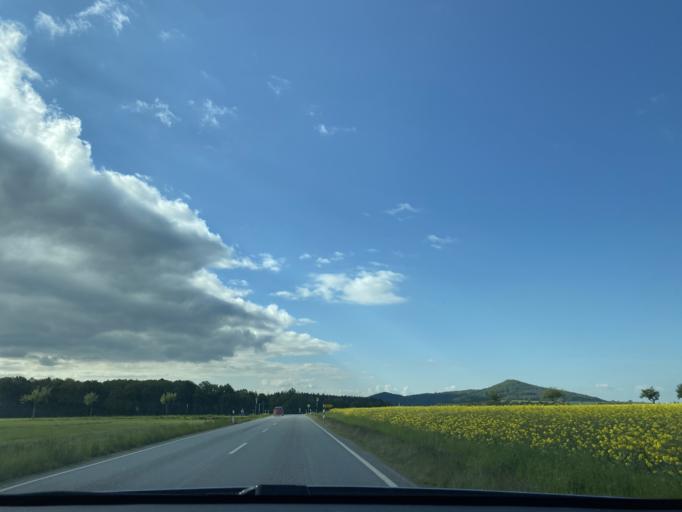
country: DE
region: Saxony
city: Sohland am Rotstein
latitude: 51.0744
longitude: 14.7737
